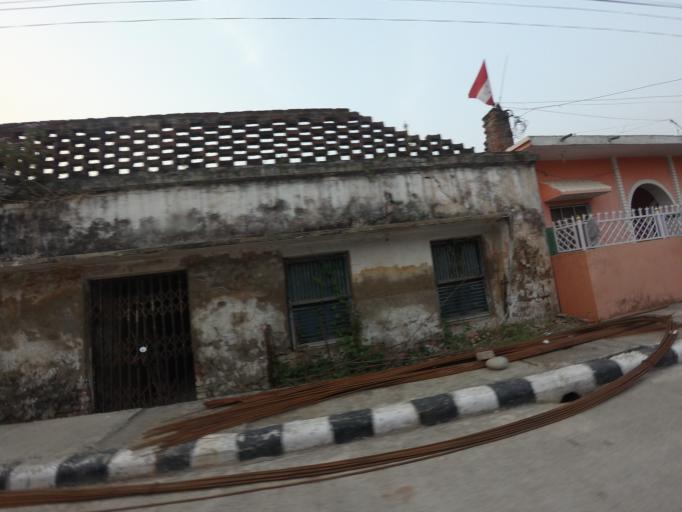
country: NP
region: Western Region
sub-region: Lumbini Zone
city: Bhairahawa
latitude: 27.5048
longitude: 83.4577
